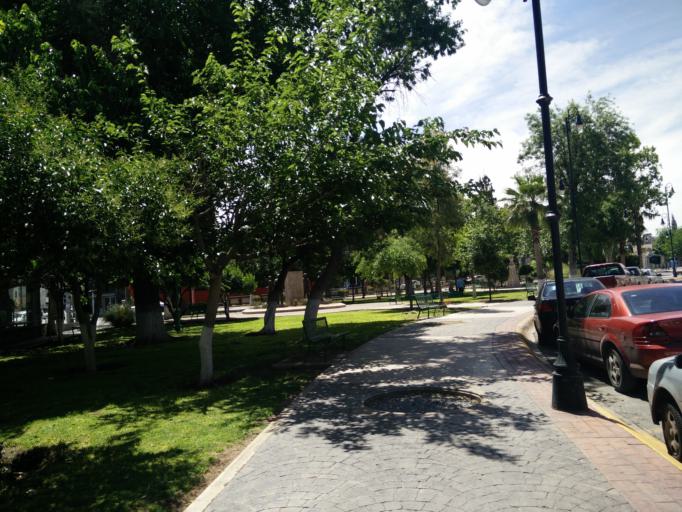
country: MX
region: Chihuahua
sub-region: Chihuahua
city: Chihuahua
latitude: 28.6338
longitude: -106.0732
